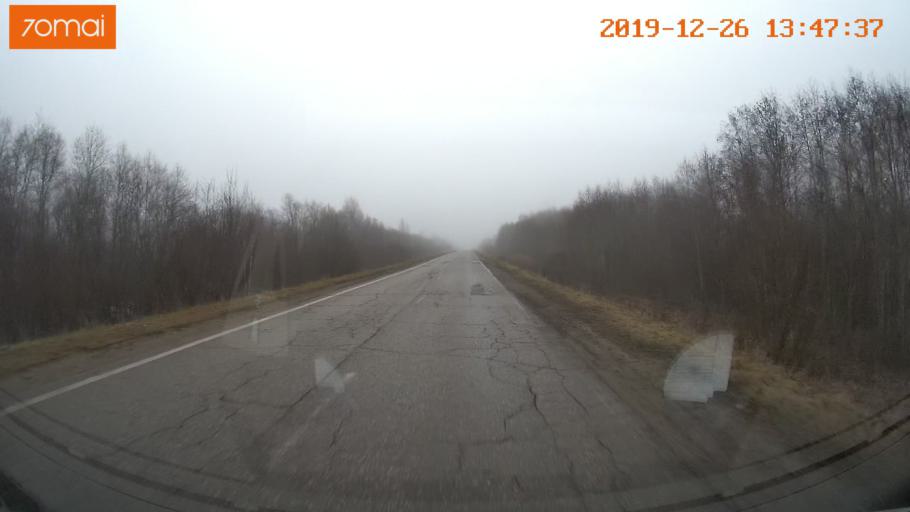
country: RU
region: Vologda
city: Sheksna
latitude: 58.6835
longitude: 38.5362
